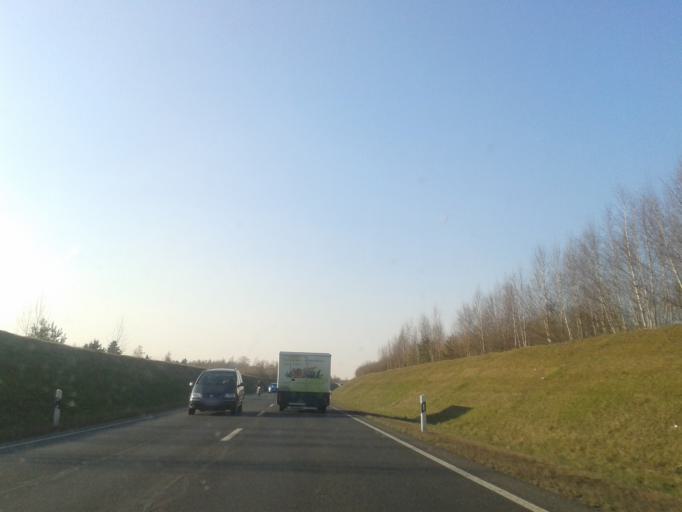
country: DE
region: Saxony
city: Nossen
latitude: 51.0265
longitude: 13.2996
